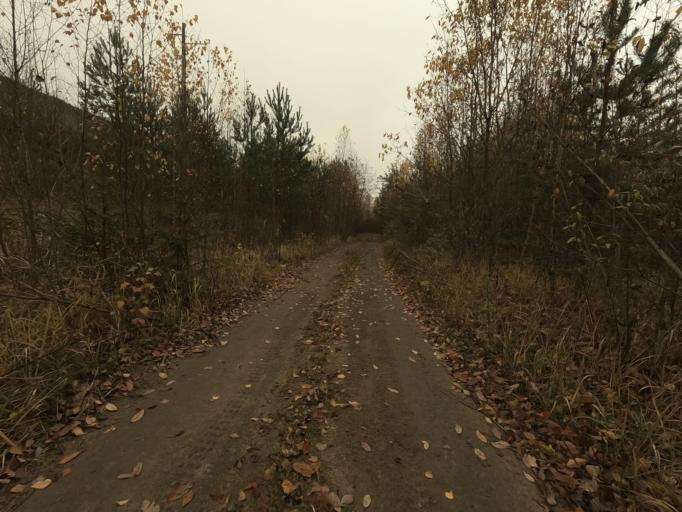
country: RU
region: Leningrad
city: Pavlovo
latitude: 59.7749
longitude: 30.9020
